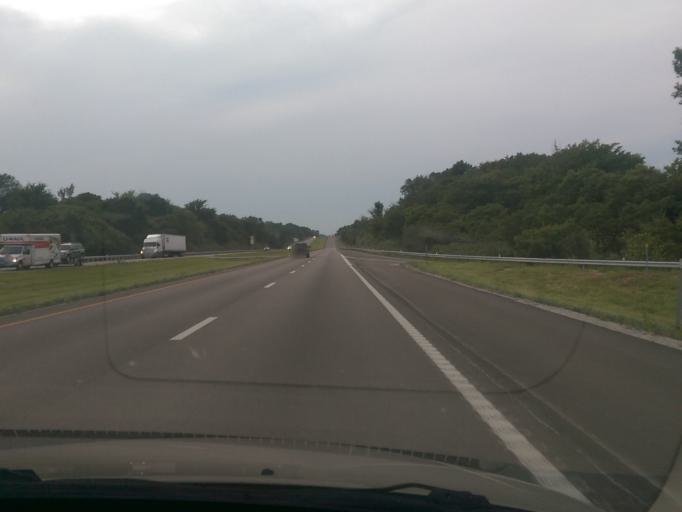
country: US
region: Missouri
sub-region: Andrew County
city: Savannah
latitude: 39.9193
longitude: -94.9088
